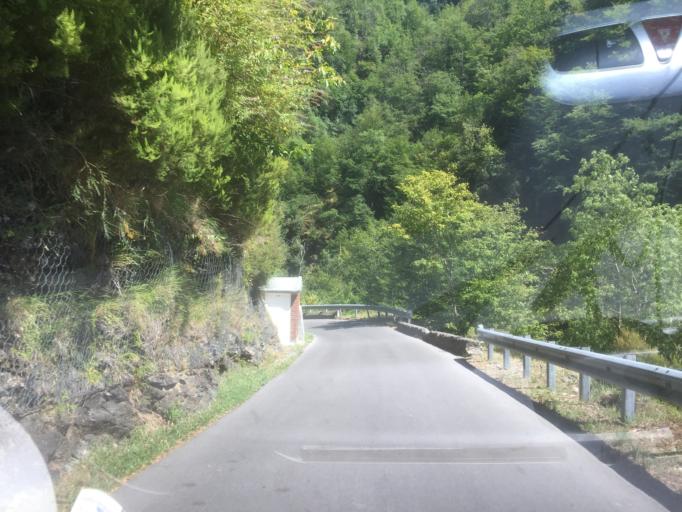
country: IT
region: Tuscany
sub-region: Provincia di Lucca
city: Molazzana
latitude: 44.0293
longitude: 10.3611
